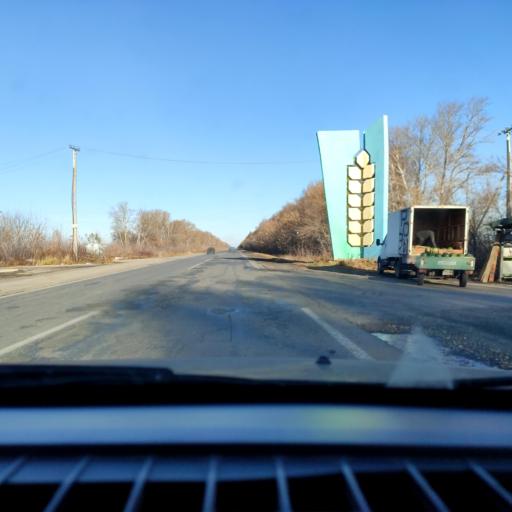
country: RU
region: Samara
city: Tol'yatti
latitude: 53.5968
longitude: 49.3251
